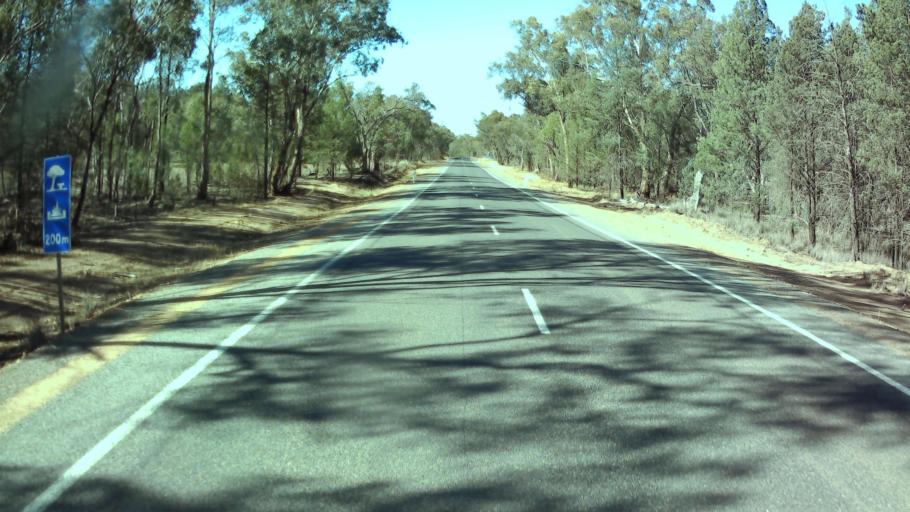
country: AU
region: New South Wales
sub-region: Weddin
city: Grenfell
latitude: -33.7494
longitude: 148.0858
